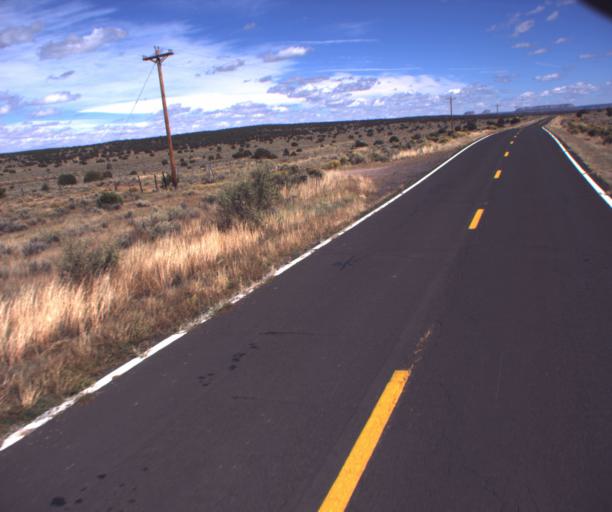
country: US
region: New Mexico
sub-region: McKinley County
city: Zuni Pueblo
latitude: 35.0026
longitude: -109.0850
